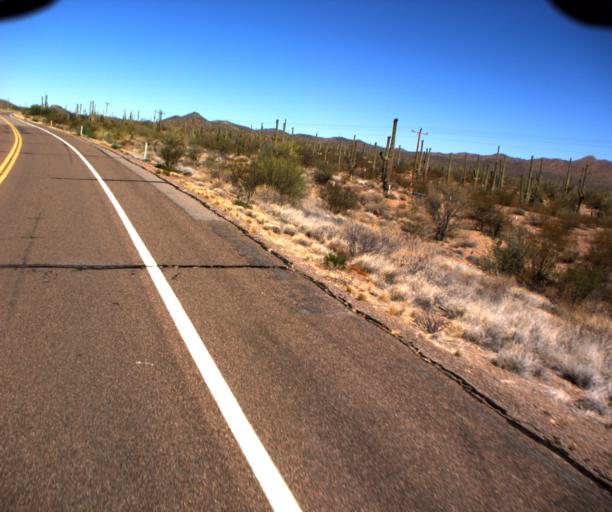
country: US
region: Arizona
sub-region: Pima County
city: Sells
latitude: 32.1656
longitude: -112.1199
